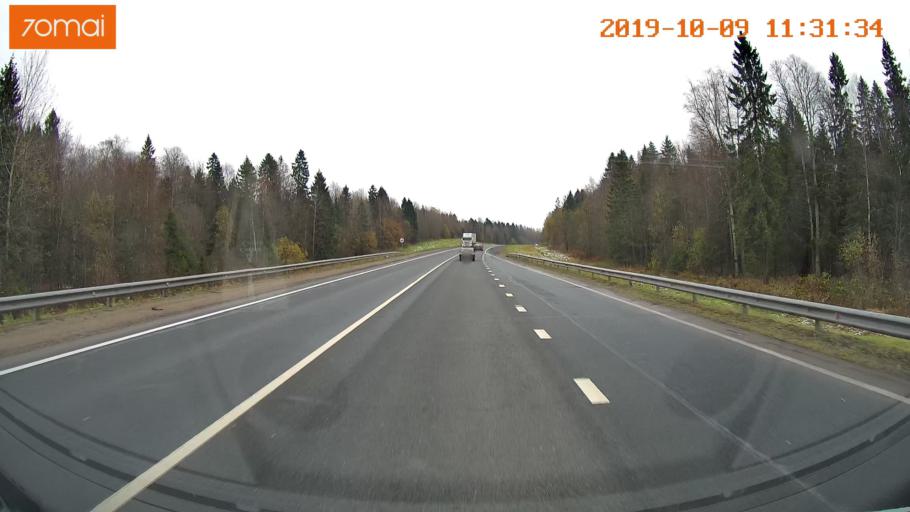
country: RU
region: Vologda
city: Gryazovets
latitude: 59.0443
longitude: 40.0986
